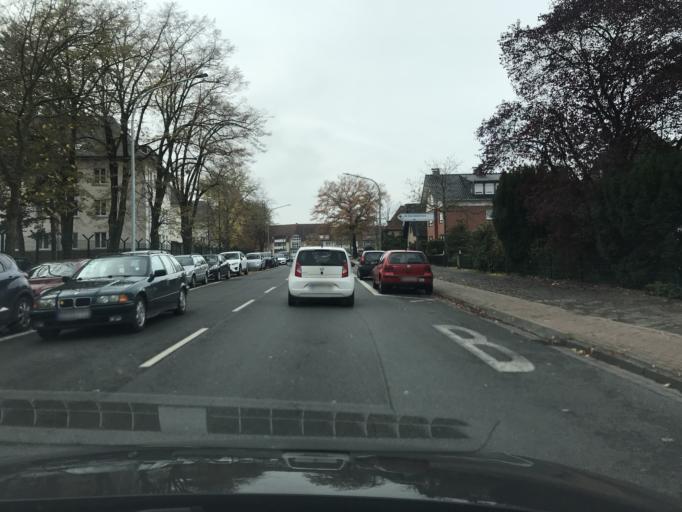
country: DE
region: North Rhine-Westphalia
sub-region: Regierungsbezirk Arnsberg
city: Hamm
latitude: 51.6910
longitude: 7.8611
